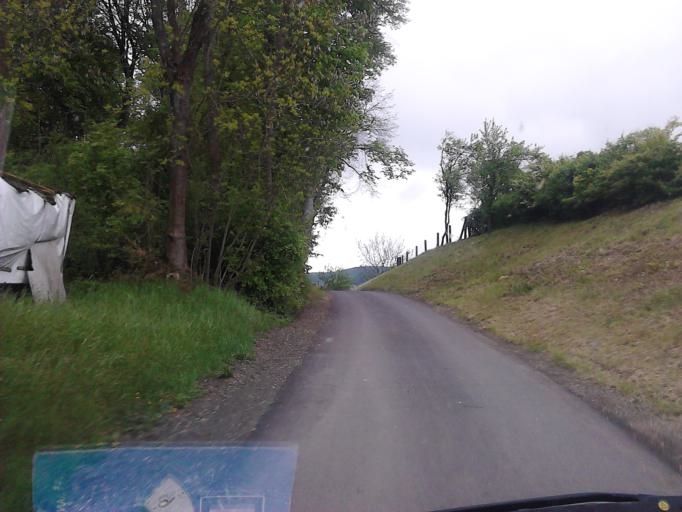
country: DE
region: Thuringia
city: Hellingen
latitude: 50.2485
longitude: 10.6846
